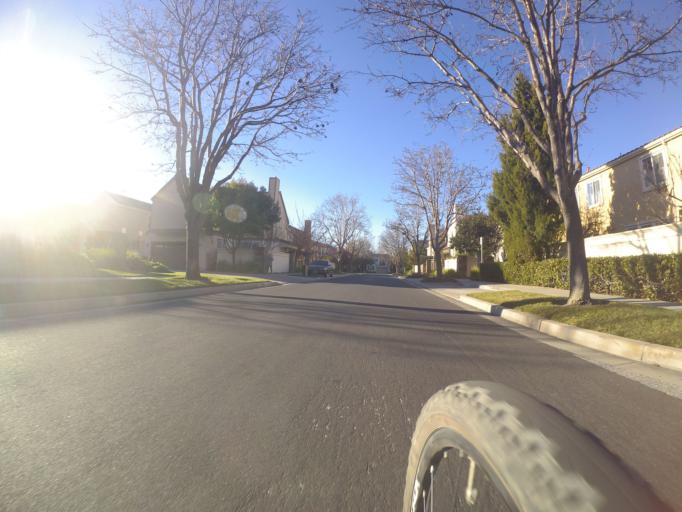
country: US
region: California
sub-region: Santa Clara County
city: Santa Clara
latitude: 37.3982
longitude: -121.9502
